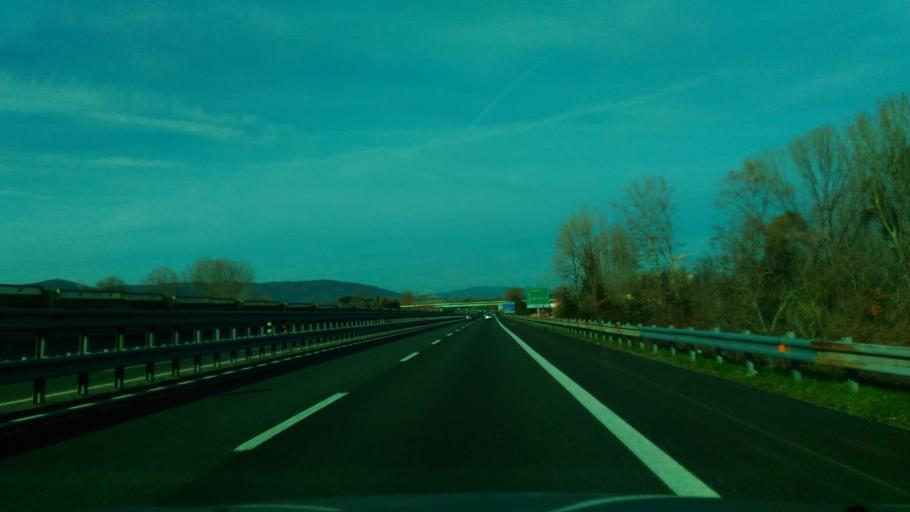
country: IT
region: Tuscany
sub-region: Provincia di Massa-Carrara
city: Marina di Carrara
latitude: 44.0488
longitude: 10.0417
